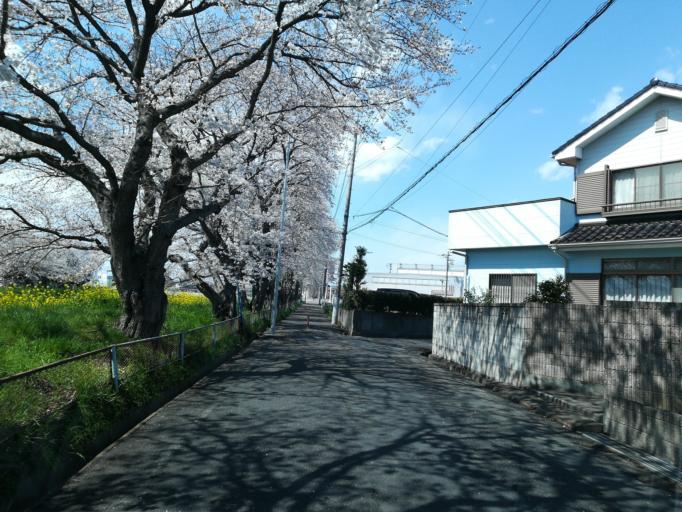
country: JP
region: Saitama
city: Kukichuo
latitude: 36.0702
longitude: 139.6915
